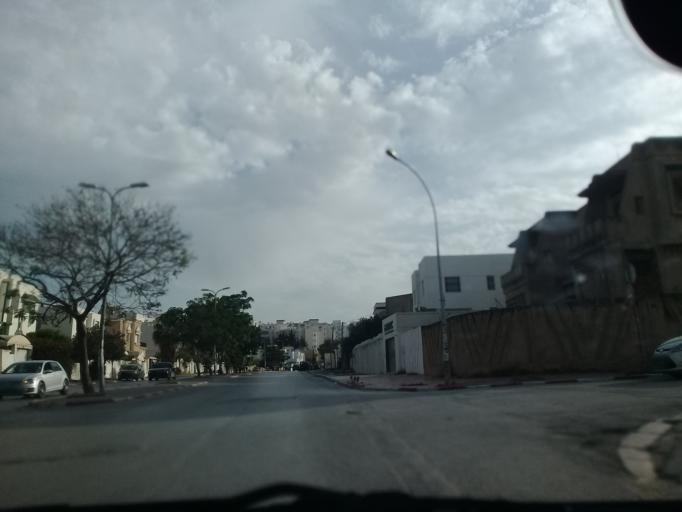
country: TN
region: Ariana
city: Ariana
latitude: 36.8620
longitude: 10.1699
